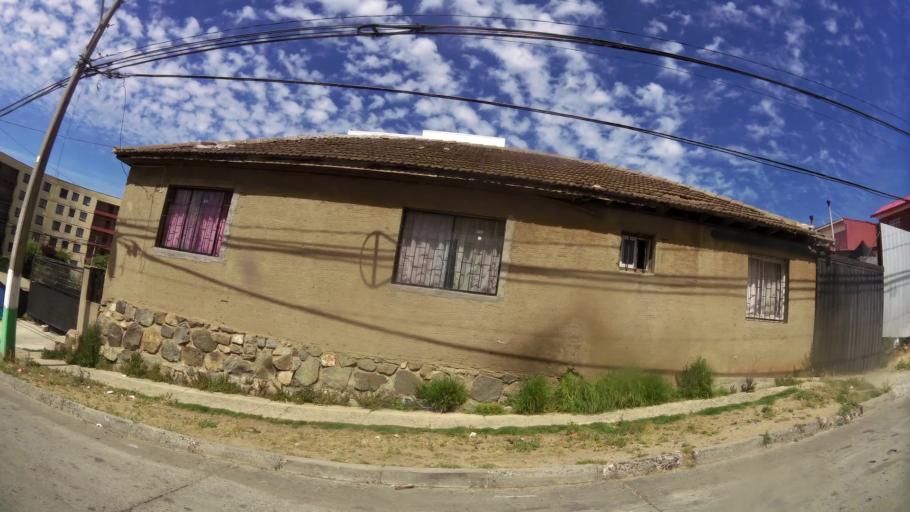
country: CL
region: Valparaiso
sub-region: Provincia de Valparaiso
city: Vina del Mar
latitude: -33.0347
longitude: -71.5825
